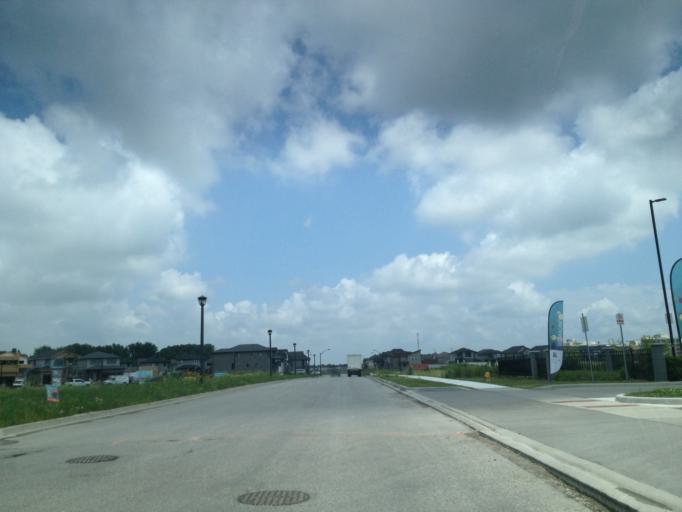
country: CA
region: Ontario
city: London
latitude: 43.0150
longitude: -81.3391
